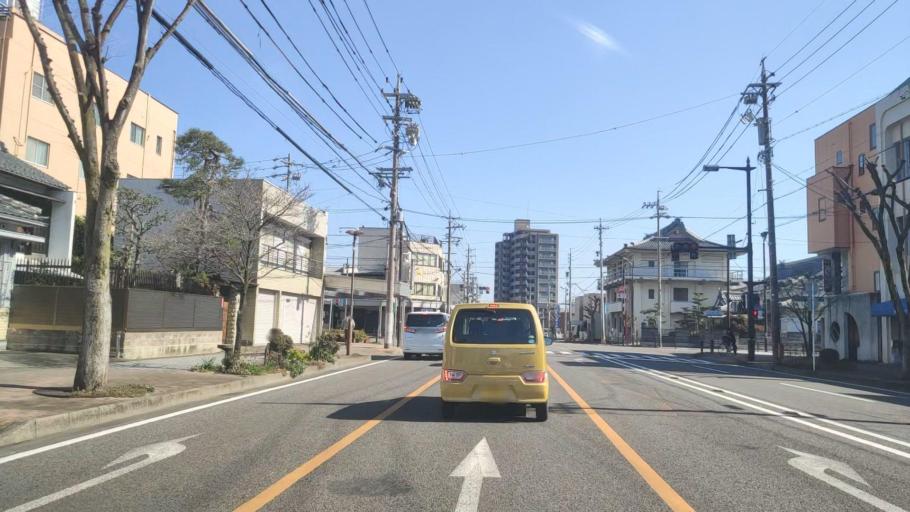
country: JP
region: Gifu
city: Gifu-shi
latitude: 35.4049
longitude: 136.7583
